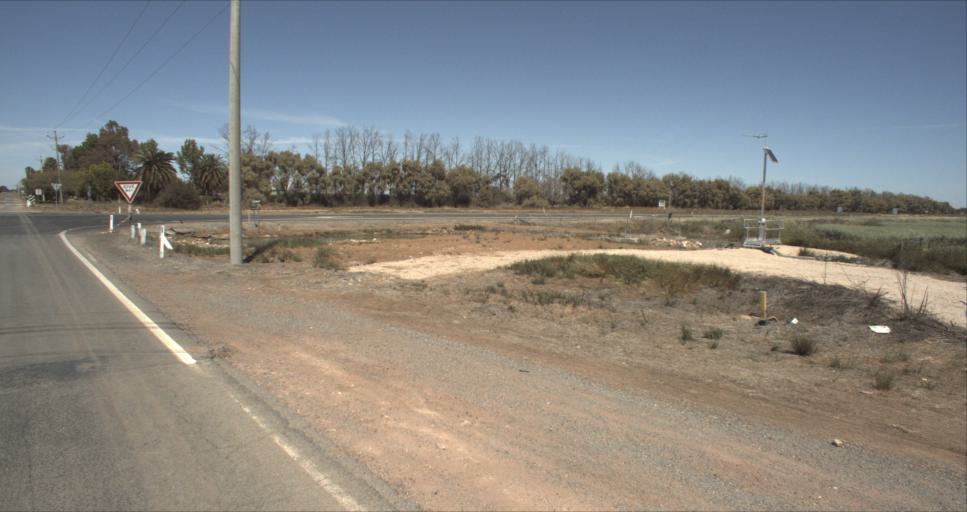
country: AU
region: New South Wales
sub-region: Leeton
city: Leeton
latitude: -34.5194
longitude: 146.2835
